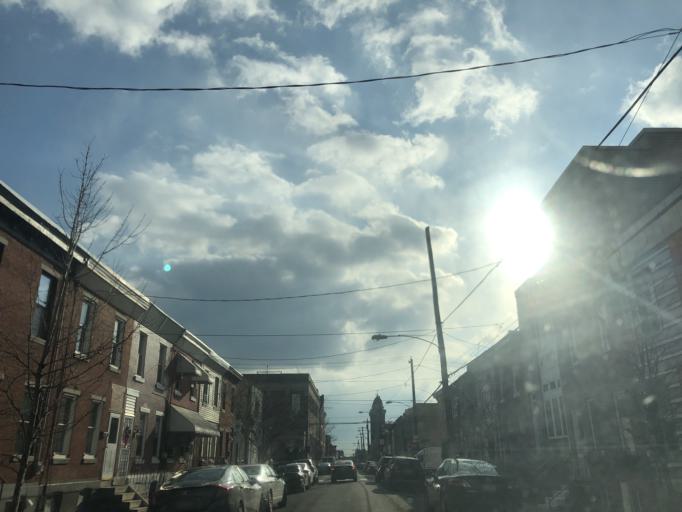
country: US
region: Pennsylvania
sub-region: Philadelphia County
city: Philadelphia
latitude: 39.9329
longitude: -75.1728
